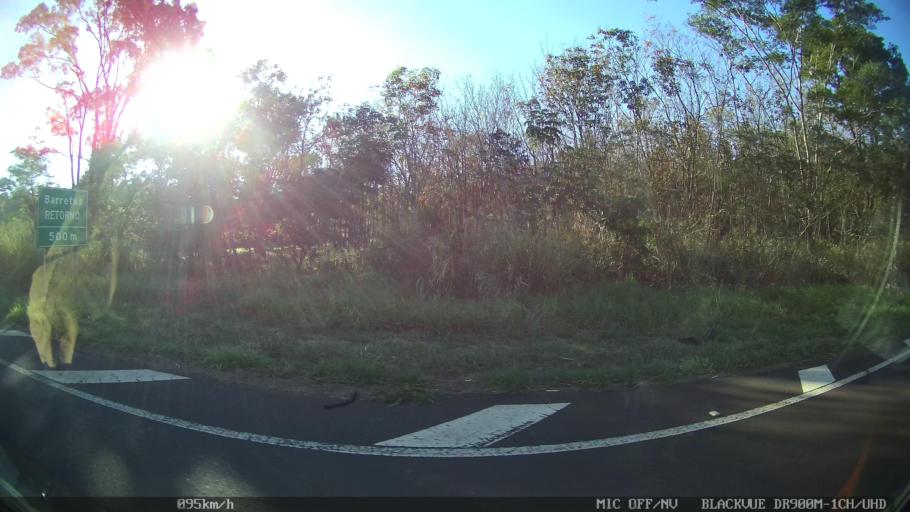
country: BR
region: Sao Paulo
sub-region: Guapiacu
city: Guapiacu
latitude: -20.7624
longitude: -49.1831
